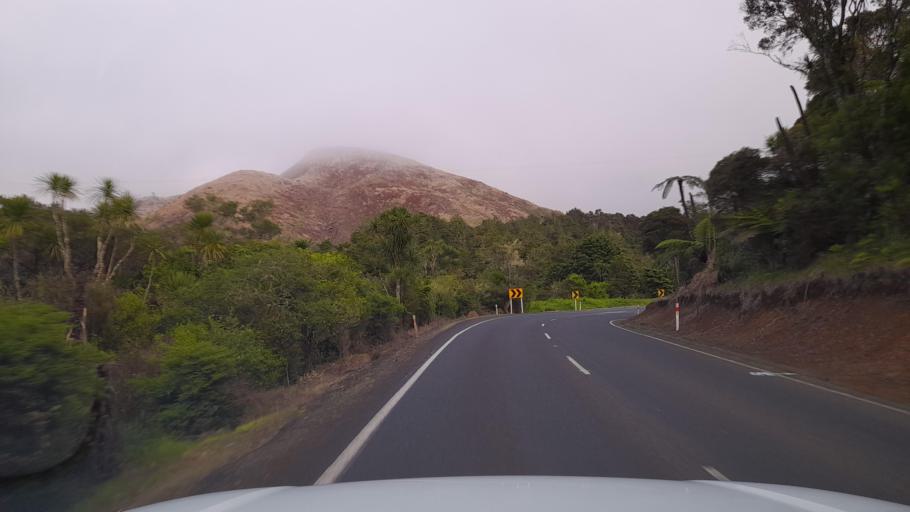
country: NZ
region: Northland
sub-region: Far North District
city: Moerewa
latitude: -35.6175
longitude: 173.8440
